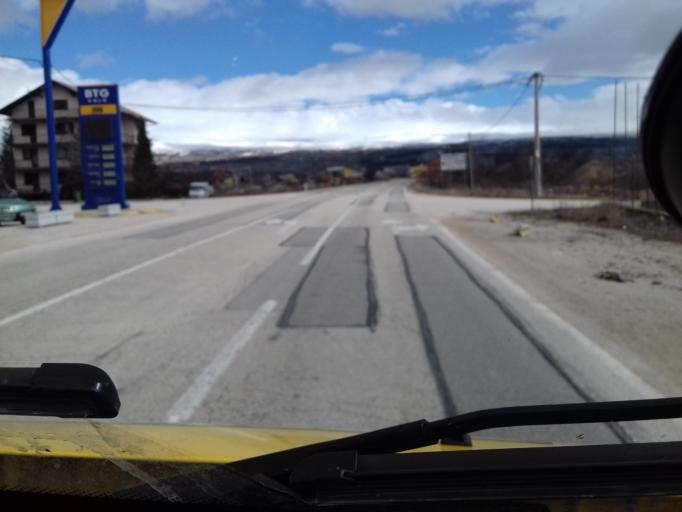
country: BA
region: Federation of Bosnia and Herzegovina
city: Tomislavgrad
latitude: 43.7070
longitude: 17.2298
